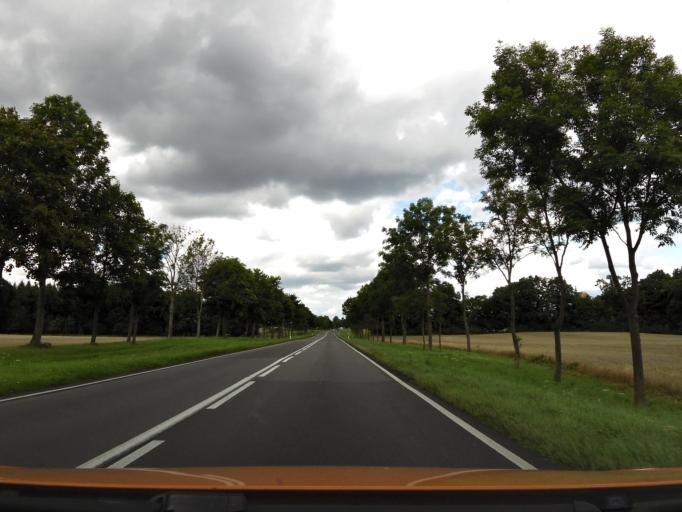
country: PL
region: West Pomeranian Voivodeship
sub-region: Powiat gryficki
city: Ploty
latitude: 53.7853
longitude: 15.2504
